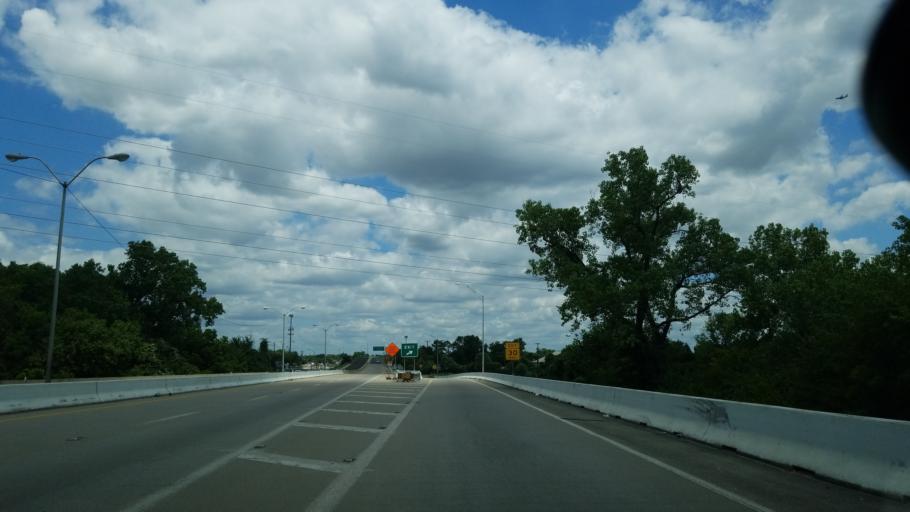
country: US
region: Texas
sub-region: Dallas County
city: Dallas
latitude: 32.7312
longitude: -96.7578
